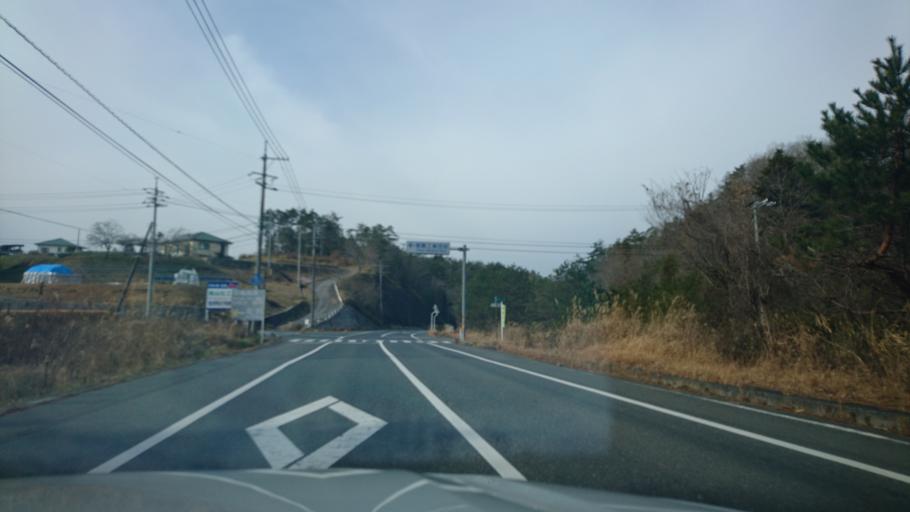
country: JP
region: Okayama
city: Takahashi
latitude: 34.8049
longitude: 133.6779
